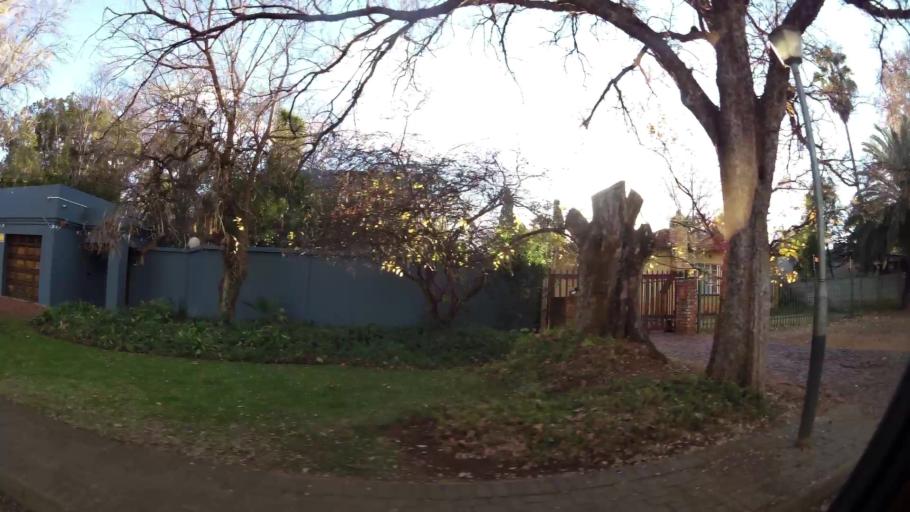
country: ZA
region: North-West
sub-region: Dr Kenneth Kaunda District Municipality
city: Potchefstroom
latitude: -26.6965
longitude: 27.0926
